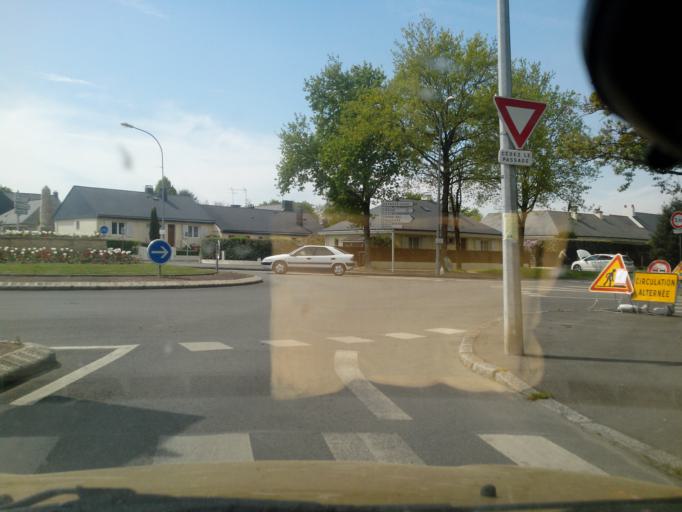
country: FR
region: Pays de la Loire
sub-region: Departement de la Loire-Atlantique
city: Orvault
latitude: 47.2545
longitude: -1.6041
